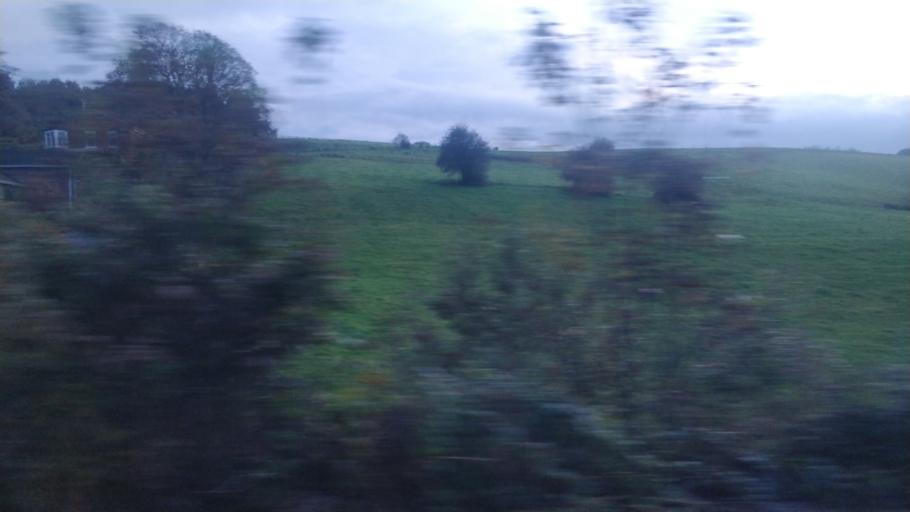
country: GB
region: England
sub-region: Borough of Wigan
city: Shevington
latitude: 53.5602
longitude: -2.6971
